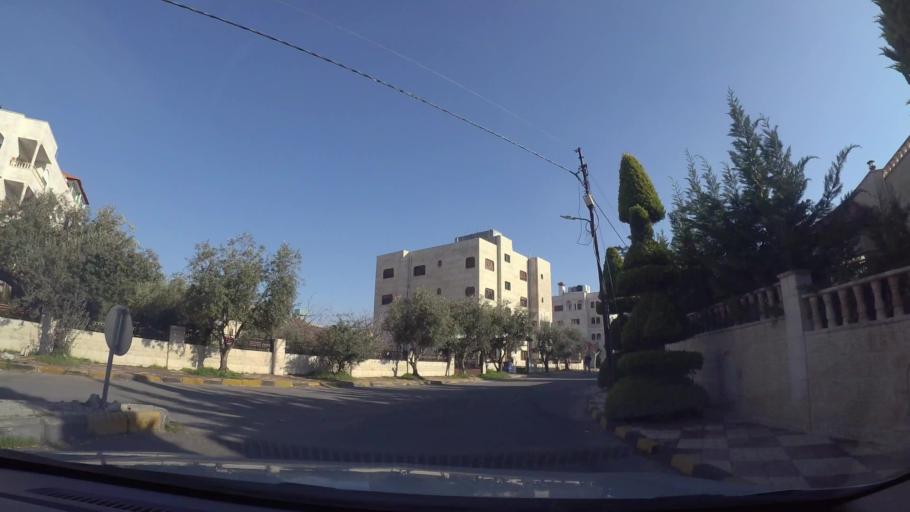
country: JO
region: Amman
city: Al Bunayyat ash Shamaliyah
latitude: 31.9006
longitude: 35.9204
